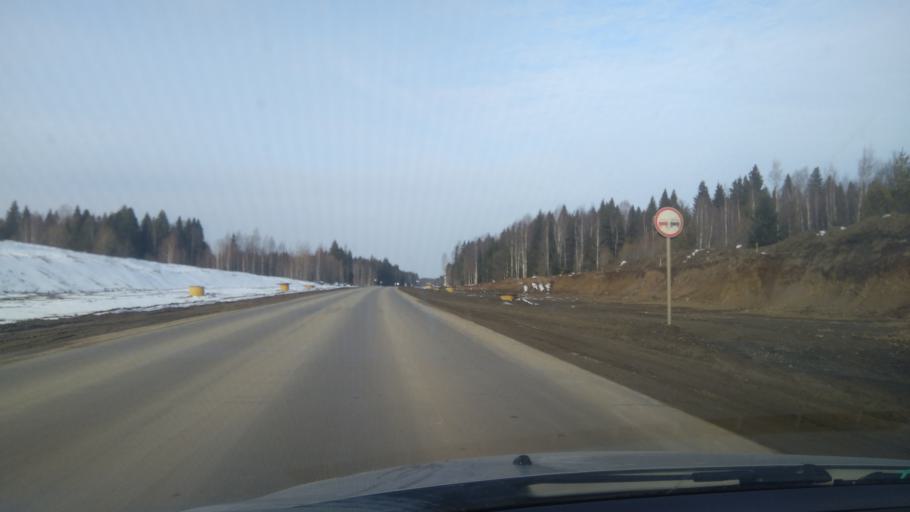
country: RU
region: Sverdlovsk
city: Bisert'
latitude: 56.8262
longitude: 59.1589
